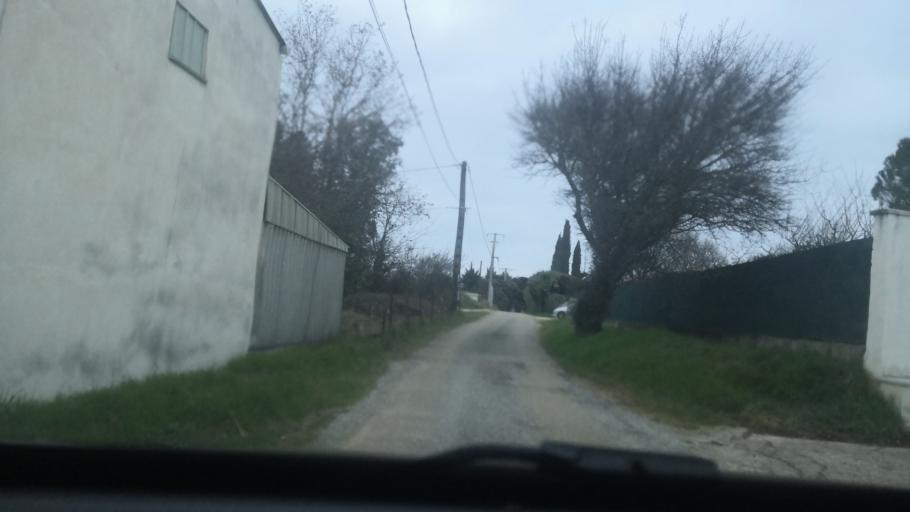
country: FR
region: Rhone-Alpes
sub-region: Departement de la Drome
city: Montboucher-sur-Jabron
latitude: 44.5543
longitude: 4.7951
